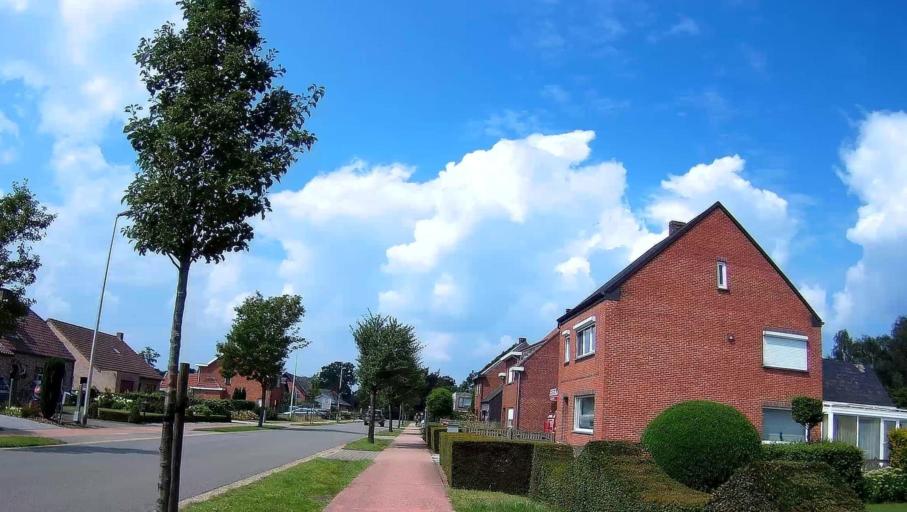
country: BE
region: Flanders
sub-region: Provincie Limburg
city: Leopoldsburg
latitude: 51.1668
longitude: 5.2822
